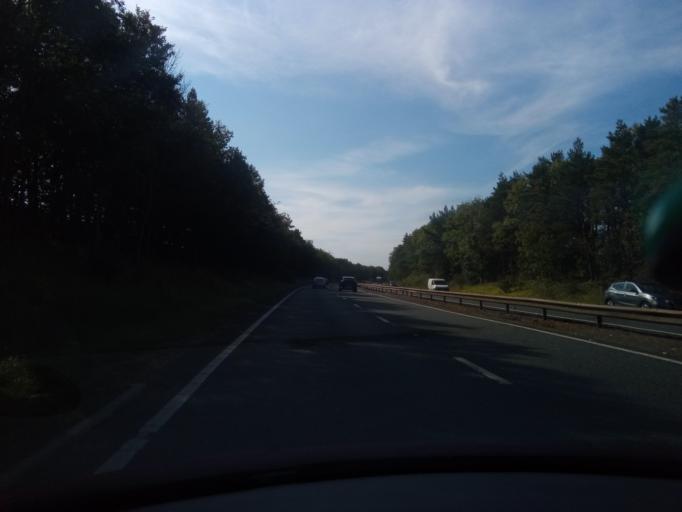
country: GB
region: England
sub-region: Redcar and Cleveland
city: Thornaby-on-Tees
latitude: 54.4876
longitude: -1.3031
